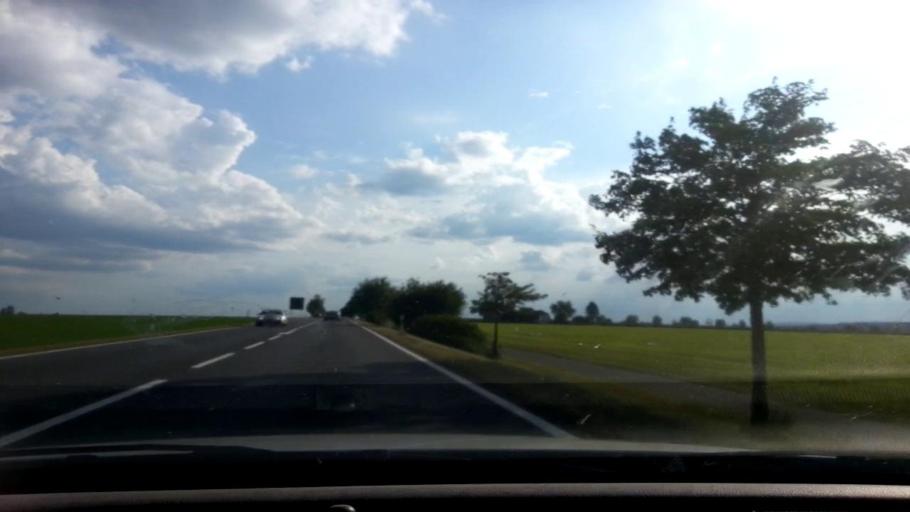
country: DE
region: Bavaria
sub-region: Upper Palatinate
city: Mitterteich
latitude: 49.9675
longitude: 12.2601
